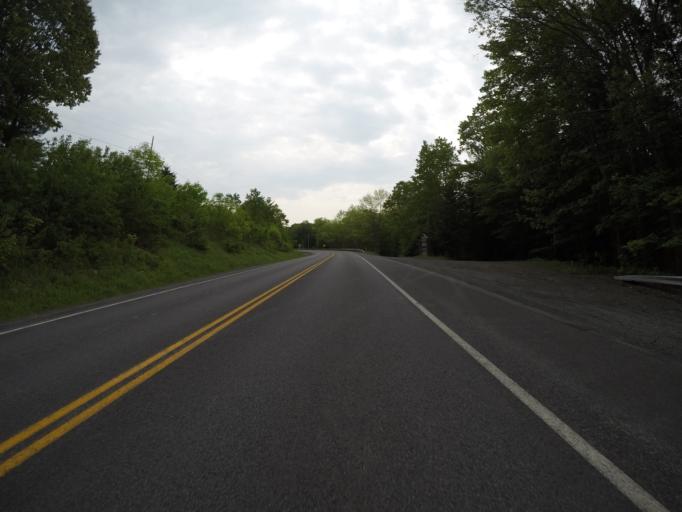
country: US
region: New York
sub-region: Sullivan County
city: Livingston Manor
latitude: 42.0607
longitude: -74.9316
